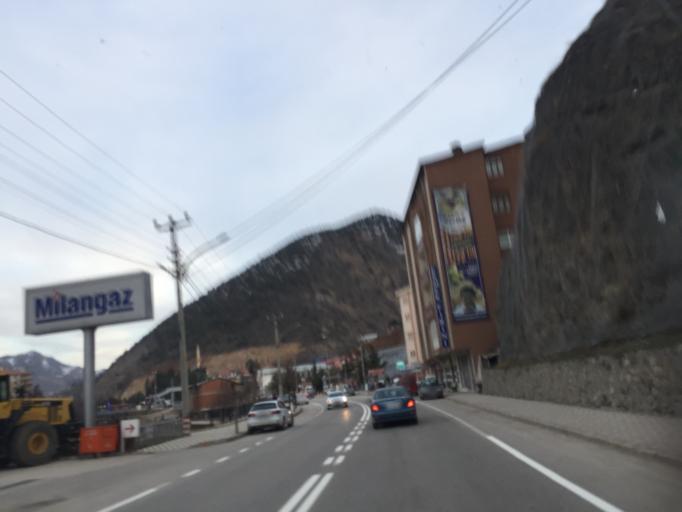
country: TR
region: Gumushane
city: Gumushkhane
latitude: 40.4630
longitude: 39.4658
